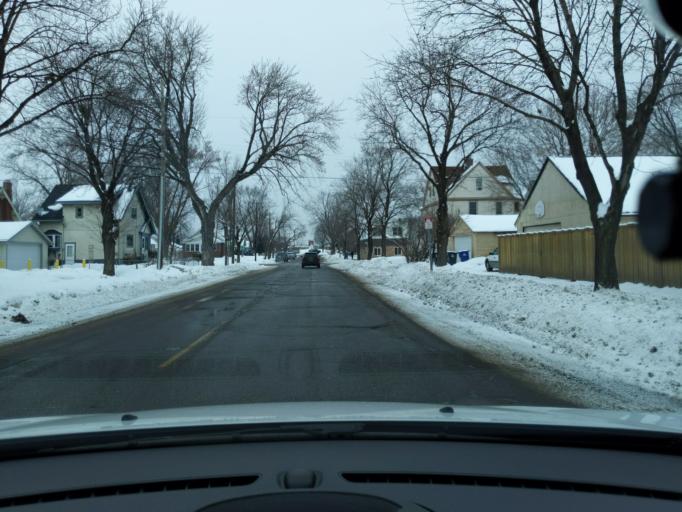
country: US
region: Minnesota
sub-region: Ramsey County
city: Falcon Heights
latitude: 44.9658
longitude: -93.1568
